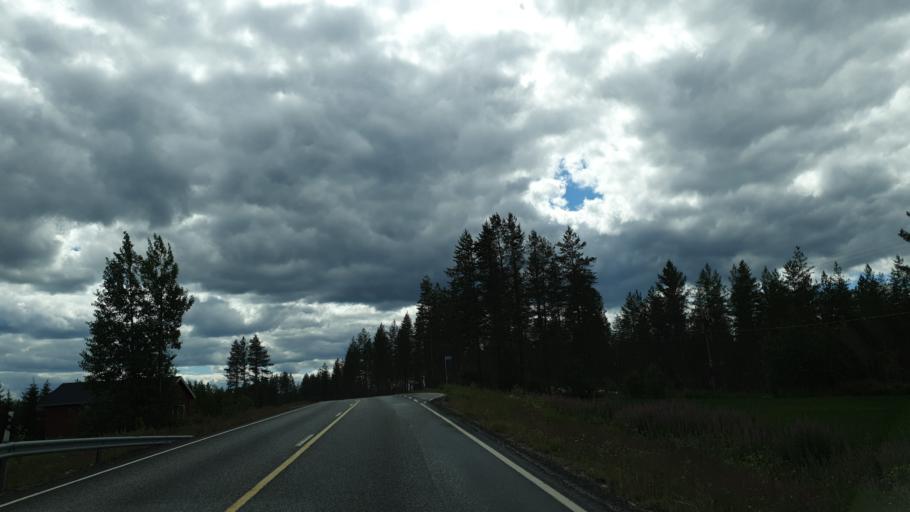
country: FI
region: Kainuu
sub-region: Kehys-Kainuu
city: Kuhmo
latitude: 64.0350
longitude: 29.5761
